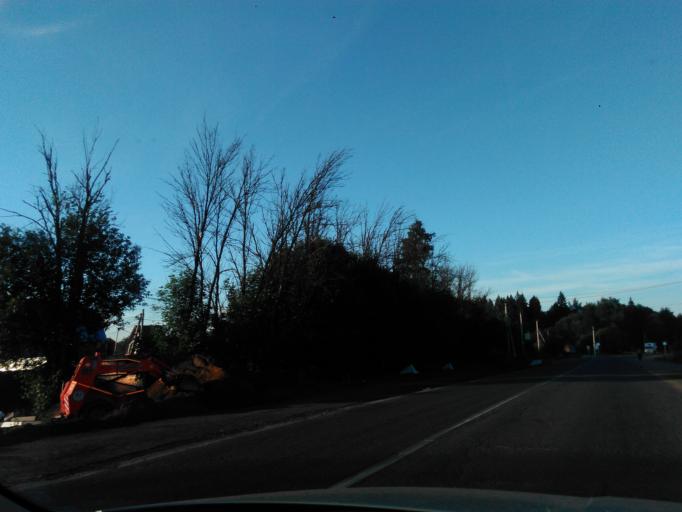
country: RU
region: Moskovskaya
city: Solnechnogorsk
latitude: 56.1438
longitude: 36.8960
